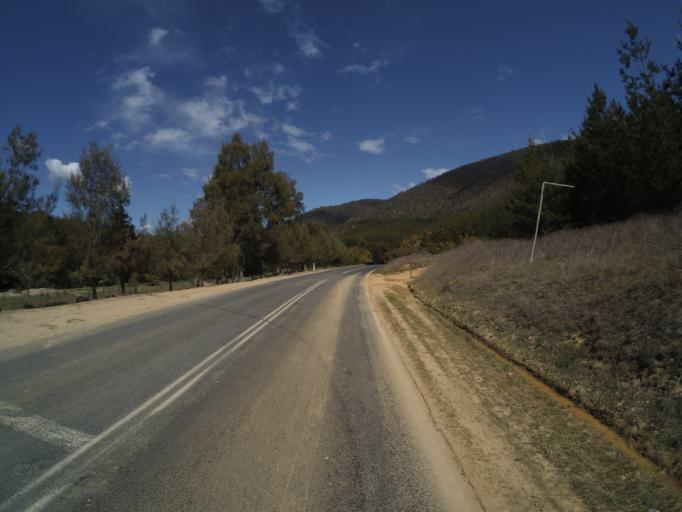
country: AU
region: Australian Capital Territory
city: Macquarie
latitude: -35.3641
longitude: 148.9521
